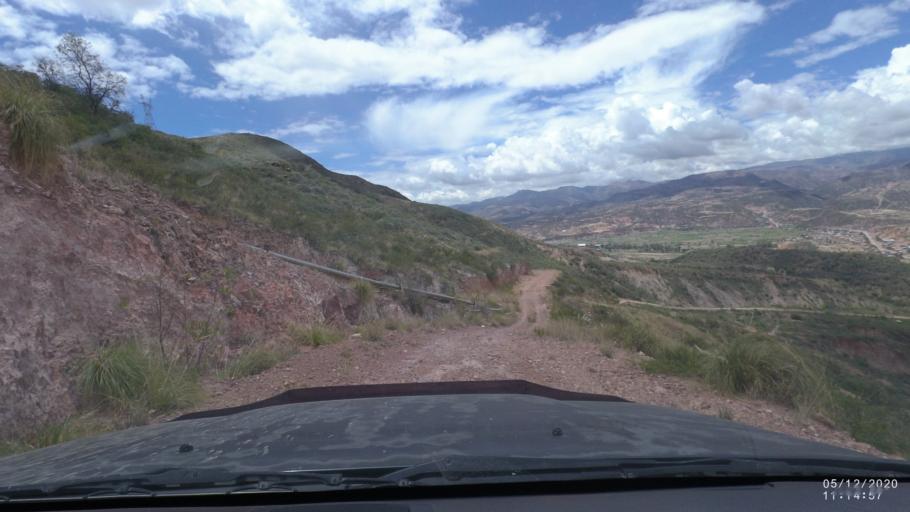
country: BO
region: Cochabamba
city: Sipe Sipe
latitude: -17.5481
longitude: -66.3298
